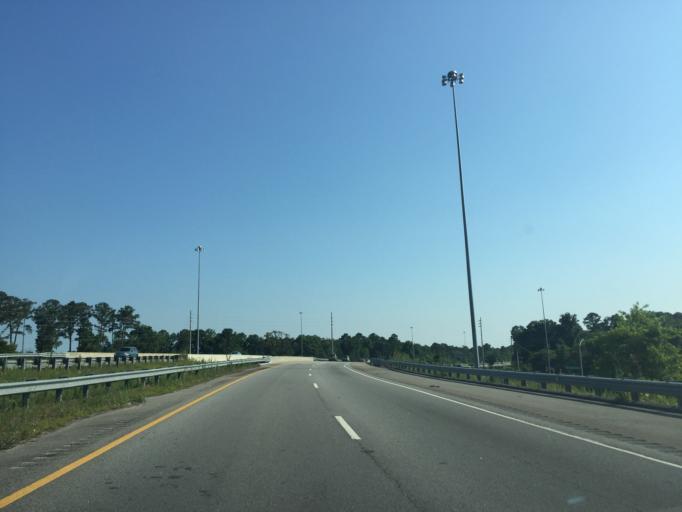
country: US
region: Georgia
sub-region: Chatham County
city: Isle of Hope
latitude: 31.9911
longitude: -81.0832
